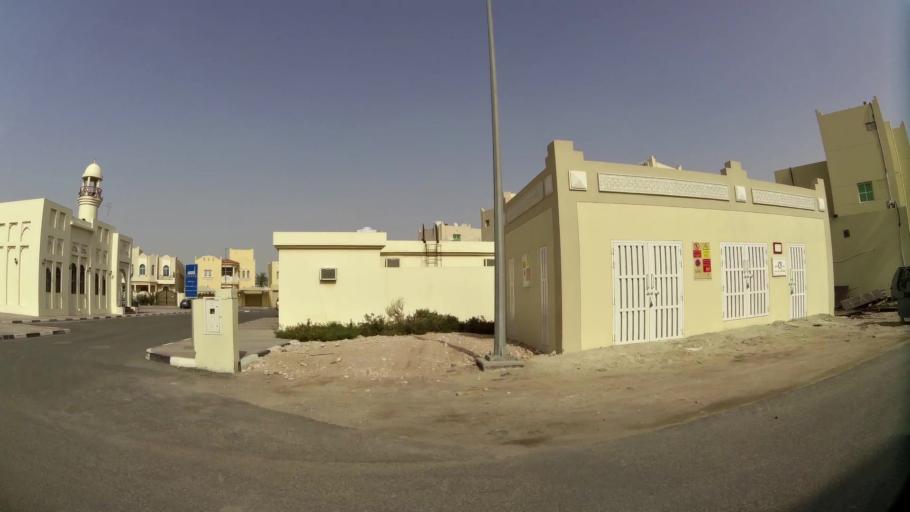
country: QA
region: Baladiyat ar Rayyan
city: Ar Rayyan
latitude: 25.2443
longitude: 51.4454
